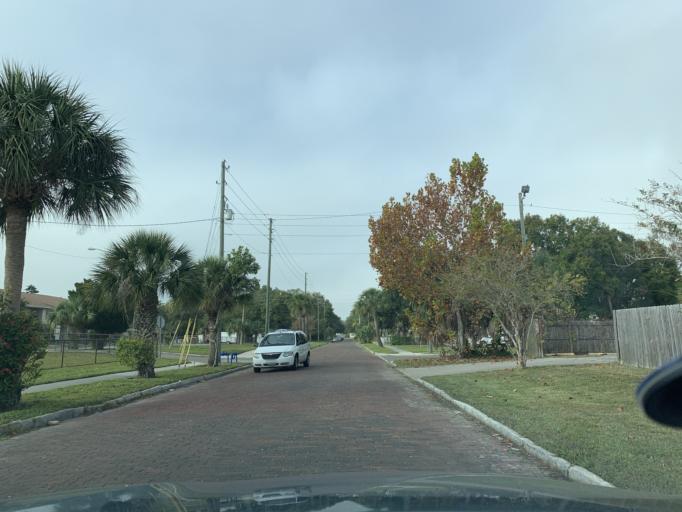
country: US
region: Florida
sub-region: Pinellas County
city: Saint Petersburg
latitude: 27.7543
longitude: -82.6391
